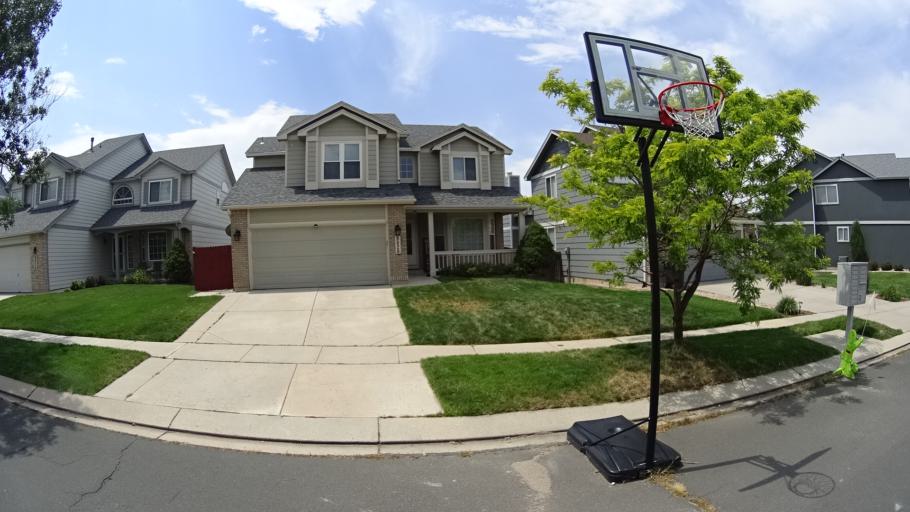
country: US
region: Colorado
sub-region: El Paso County
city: Black Forest
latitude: 38.9614
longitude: -104.7701
